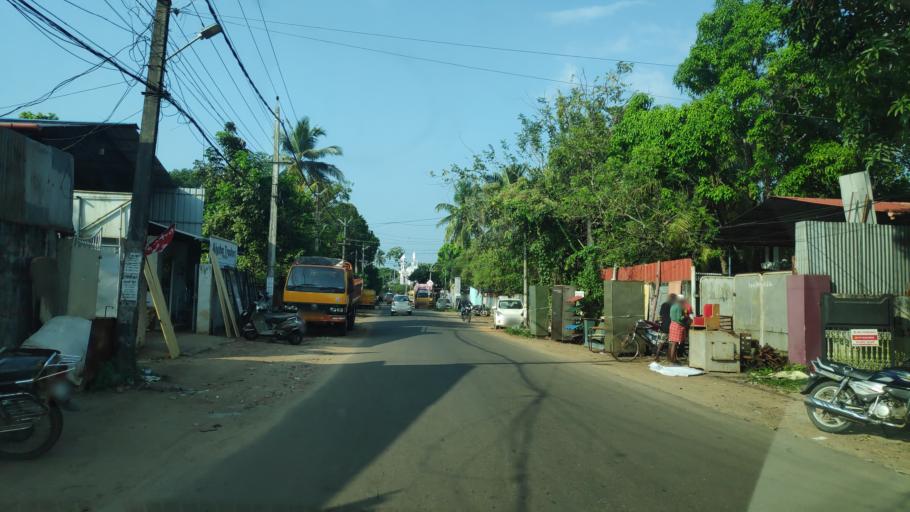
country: IN
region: Kerala
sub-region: Alappuzha
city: Alleppey
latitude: 9.4833
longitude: 76.3340
